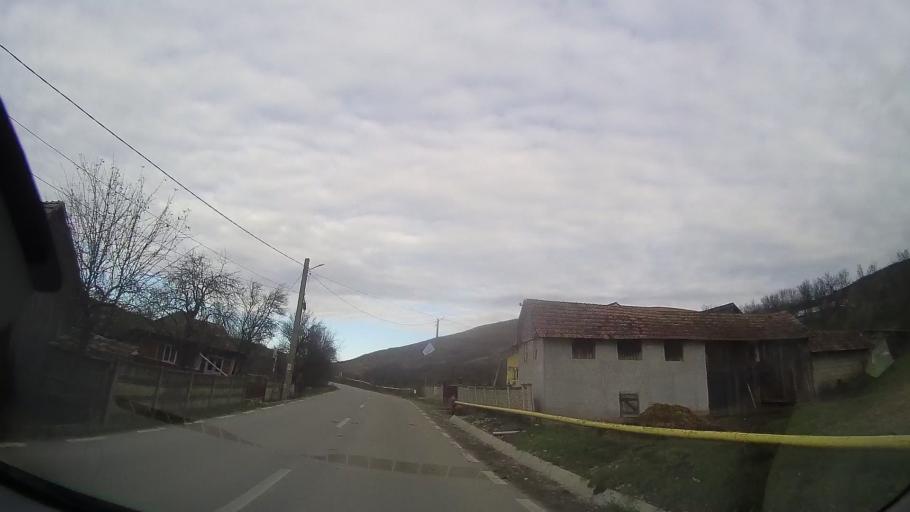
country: RO
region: Cluj
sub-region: Comuna Geaca
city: Geaca
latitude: 46.8414
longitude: 24.1363
